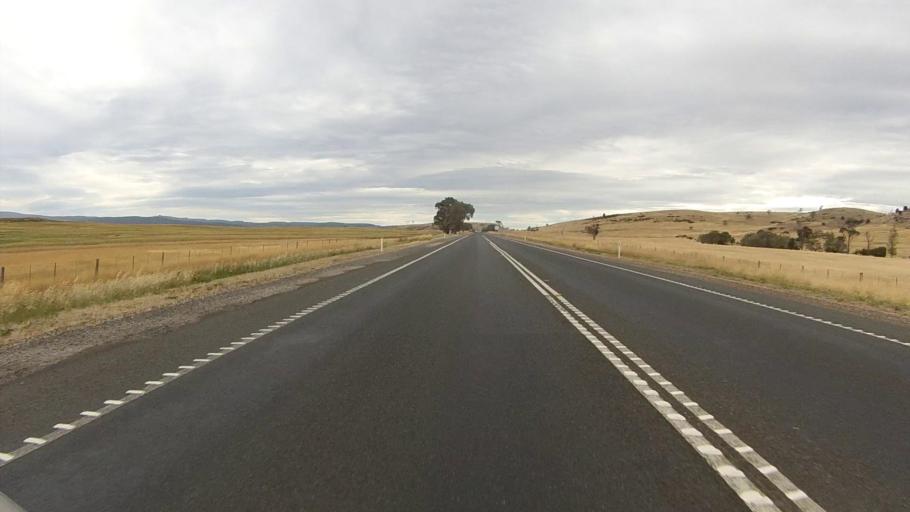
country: AU
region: Tasmania
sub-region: Brighton
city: Bridgewater
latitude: -42.3637
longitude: 147.3358
